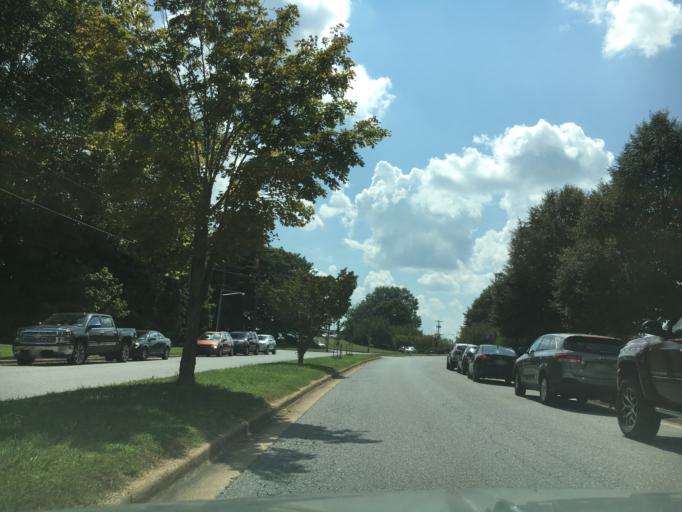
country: US
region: Virginia
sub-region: City of Lynchburg
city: West Lynchburg
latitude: 37.4165
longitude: -79.1698
